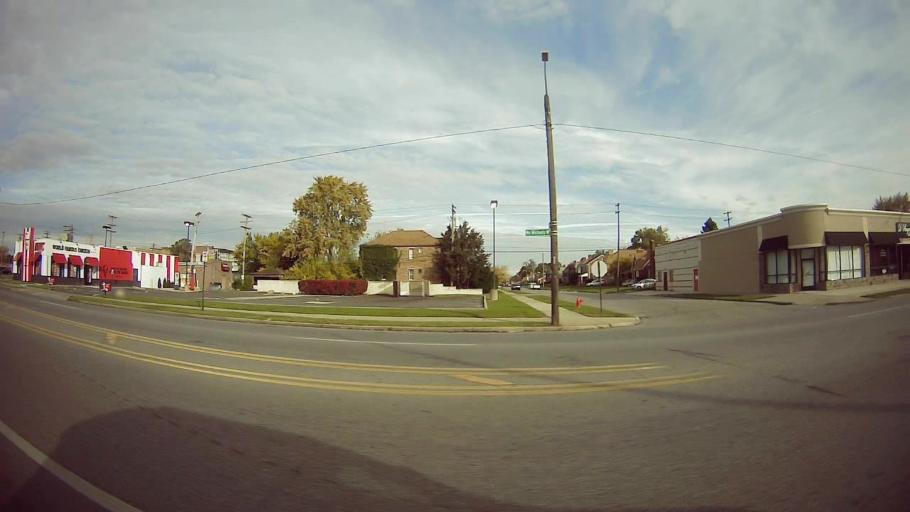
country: US
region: Michigan
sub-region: Oakland County
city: Oak Park
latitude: 42.4166
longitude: -83.1788
